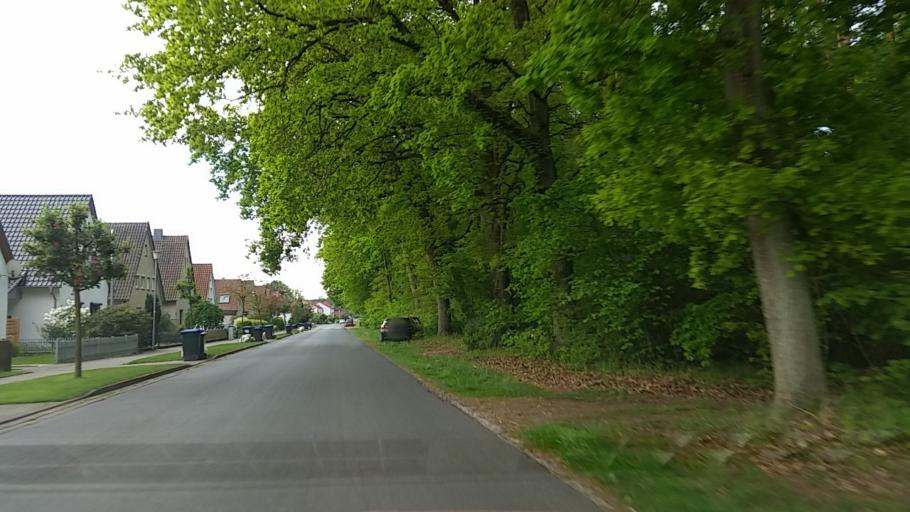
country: DE
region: Lower Saxony
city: Bodenteich
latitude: 52.8391
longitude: 10.6738
